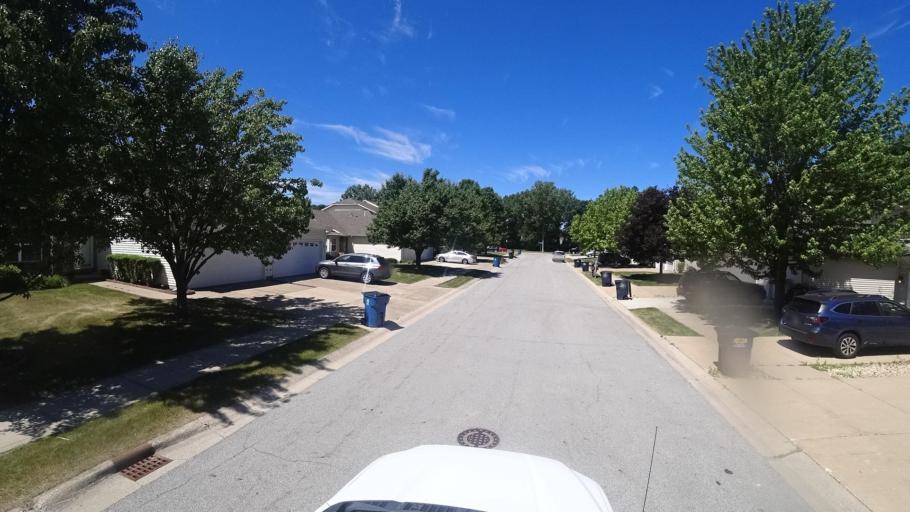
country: US
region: Indiana
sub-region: Porter County
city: Porter
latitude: 41.6325
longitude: -87.0706
